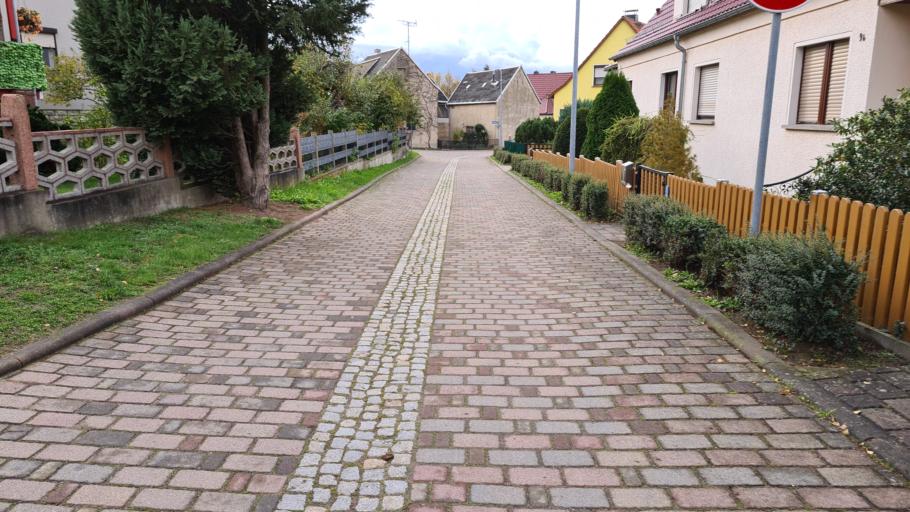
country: DE
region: Saxony
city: Dahlen
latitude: 51.4001
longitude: 12.9877
